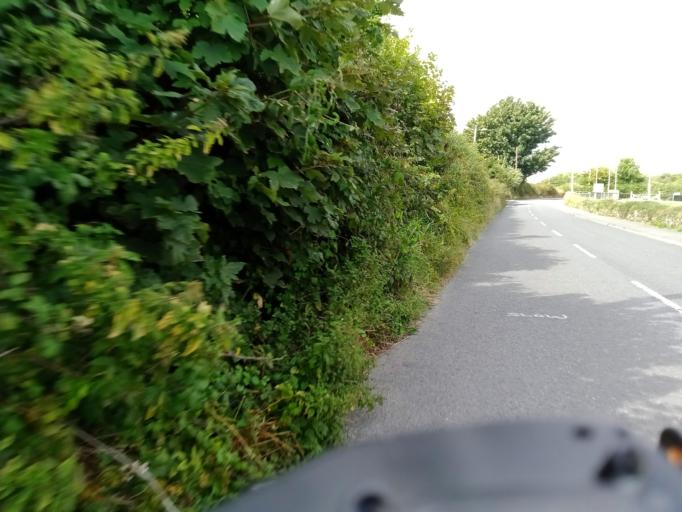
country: IE
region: Munster
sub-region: Waterford
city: Dungarvan
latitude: 52.1329
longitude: -7.4645
